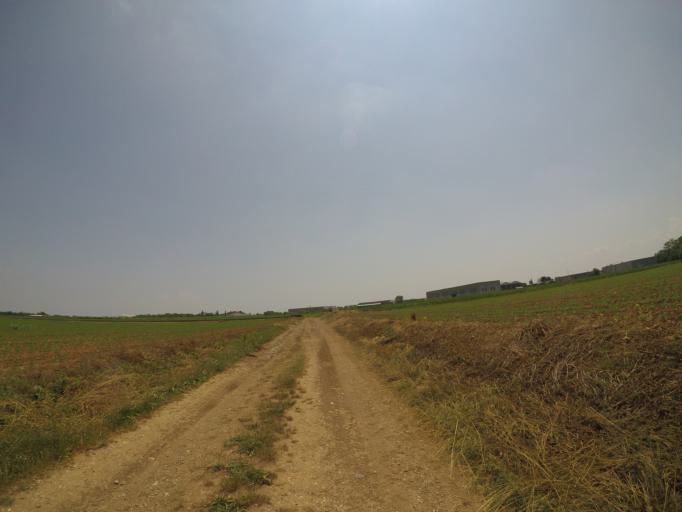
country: IT
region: Friuli Venezia Giulia
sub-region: Provincia di Udine
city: Bertiolo
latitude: 45.9538
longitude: 13.0599
